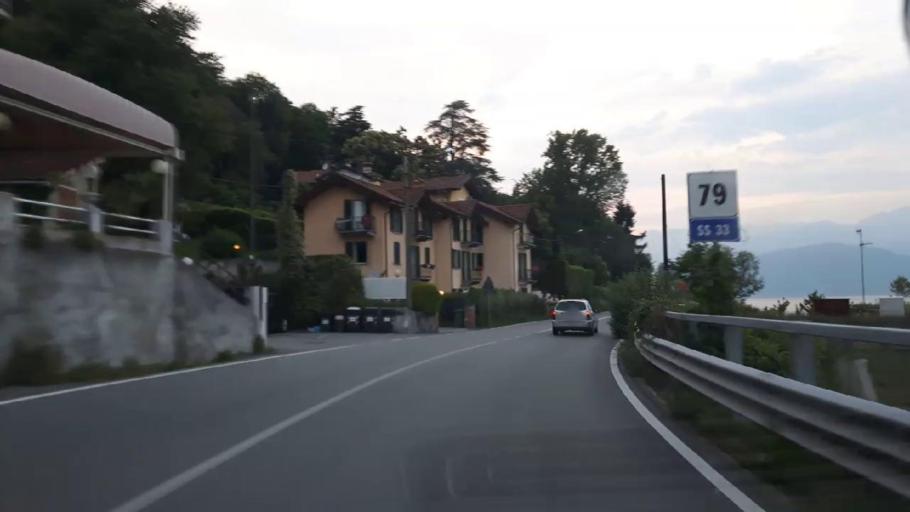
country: IT
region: Piedmont
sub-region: Provincia Verbano-Cusio-Ossola
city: Stresa
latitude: 45.8715
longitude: 8.5634
